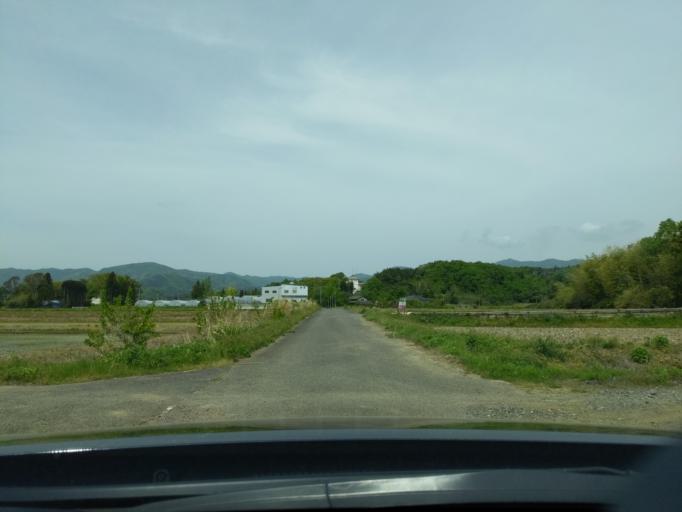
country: JP
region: Fukushima
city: Koriyama
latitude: 37.4057
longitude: 140.2764
